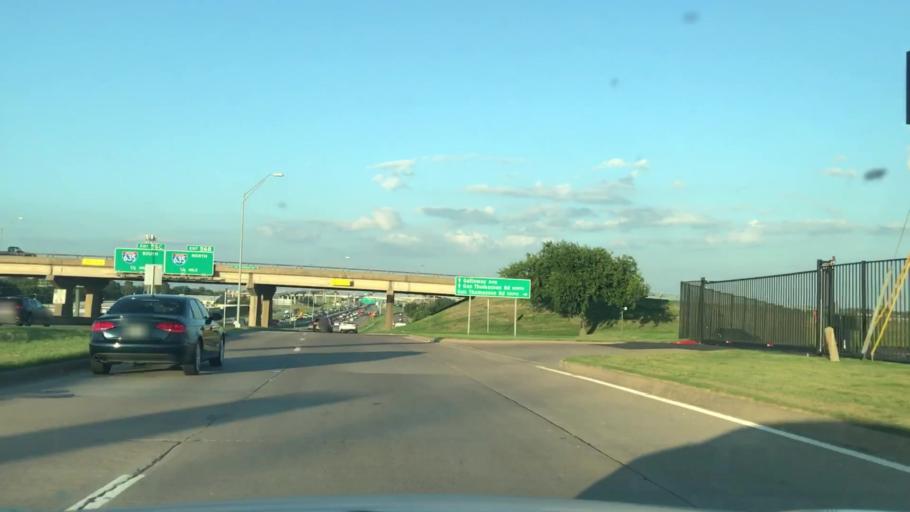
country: US
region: Texas
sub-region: Dallas County
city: Mesquite
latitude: 32.8168
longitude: -96.6397
